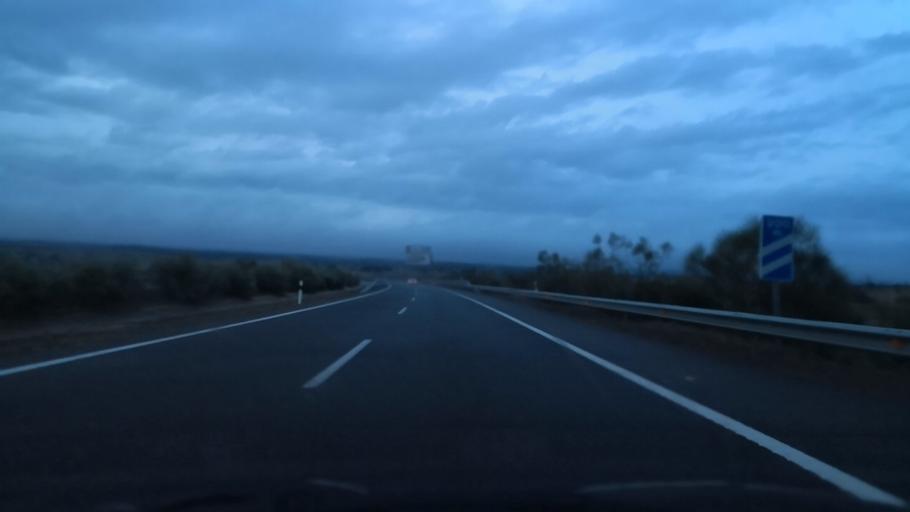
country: ES
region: Extremadura
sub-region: Provincia de Badajoz
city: Merida
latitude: 38.9710
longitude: -6.3353
